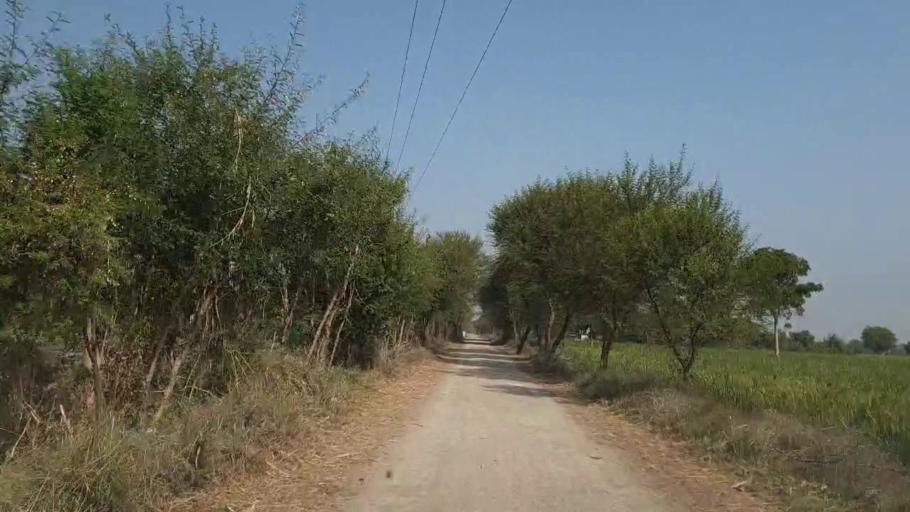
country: PK
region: Sindh
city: Mirpur Khas
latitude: 25.5826
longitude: 69.0126
